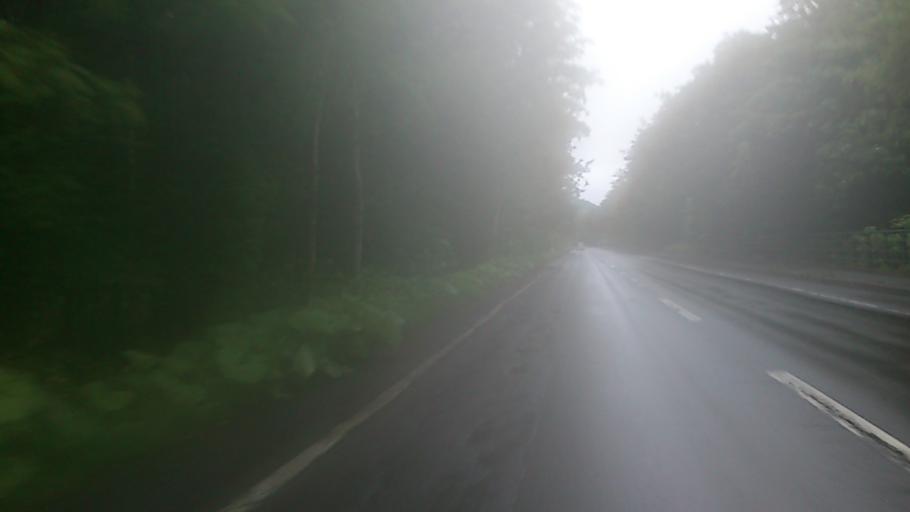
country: JP
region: Hokkaido
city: Tomakomai
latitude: 42.7632
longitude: 141.4328
